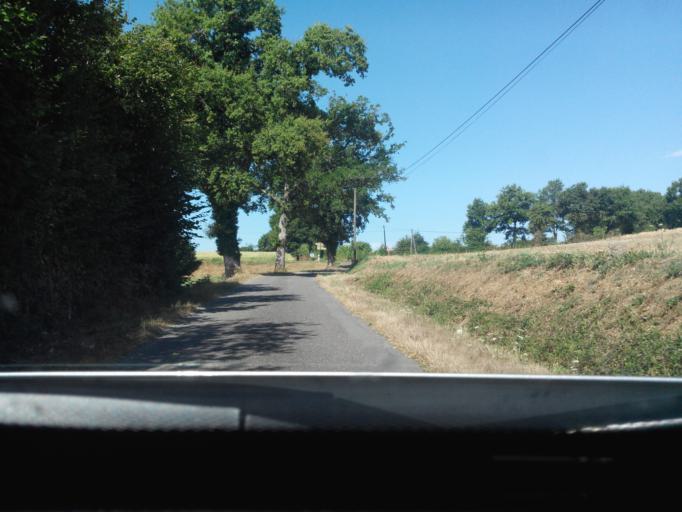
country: FR
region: Poitou-Charentes
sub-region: Departement de la Charente
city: Etagnac
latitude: 45.9372
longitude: 0.7722
